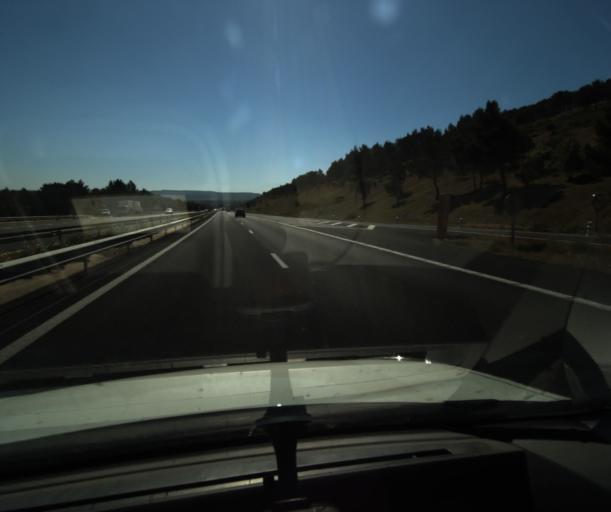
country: FR
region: Languedoc-Roussillon
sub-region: Departement de l'Aude
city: Narbonne
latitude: 43.1540
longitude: 2.9591
